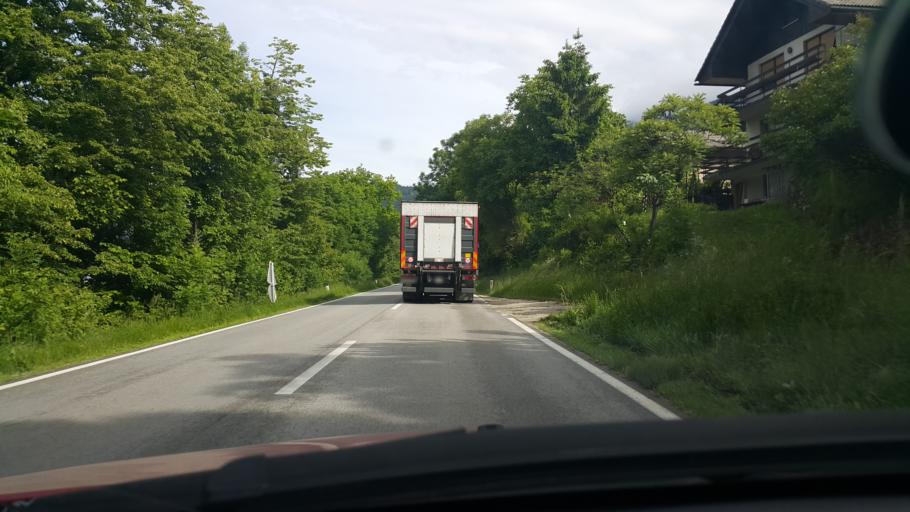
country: SI
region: Zirovnica
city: Zirovnica
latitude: 46.3994
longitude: 14.1360
